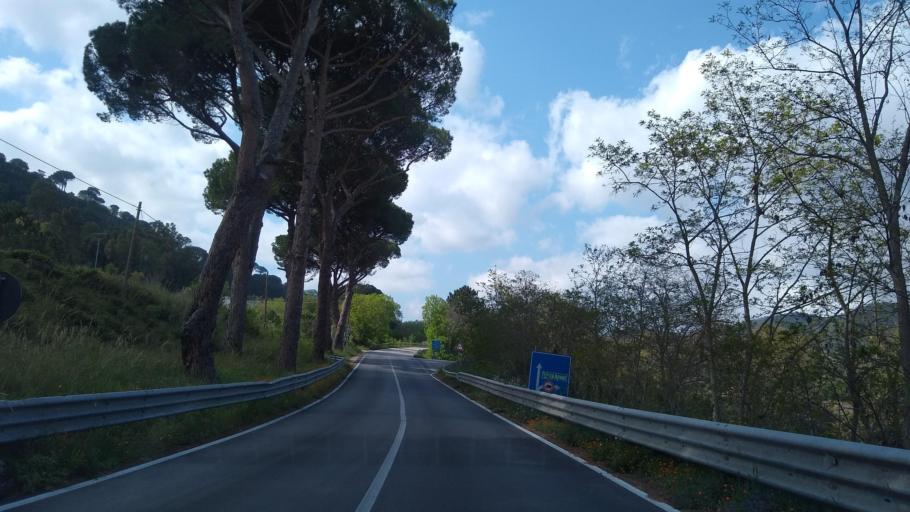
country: IT
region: Sicily
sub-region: Trapani
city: Calatafimi
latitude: 37.9365
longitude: 12.8538
